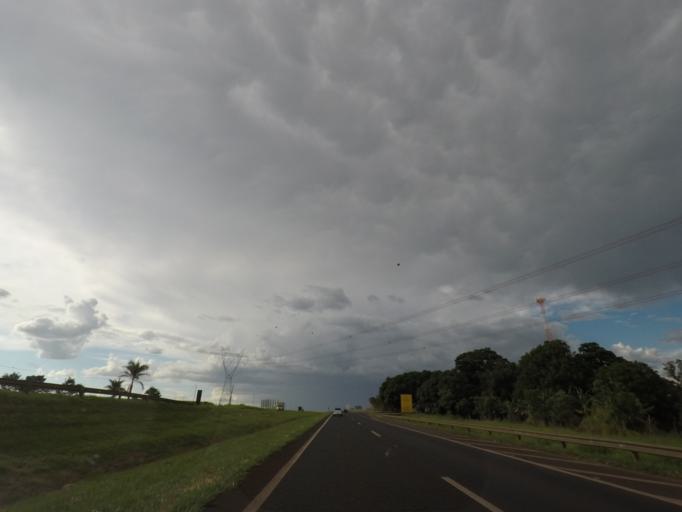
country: BR
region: Sao Paulo
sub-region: Jardinopolis
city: Jardinopolis
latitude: -21.0394
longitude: -47.8307
